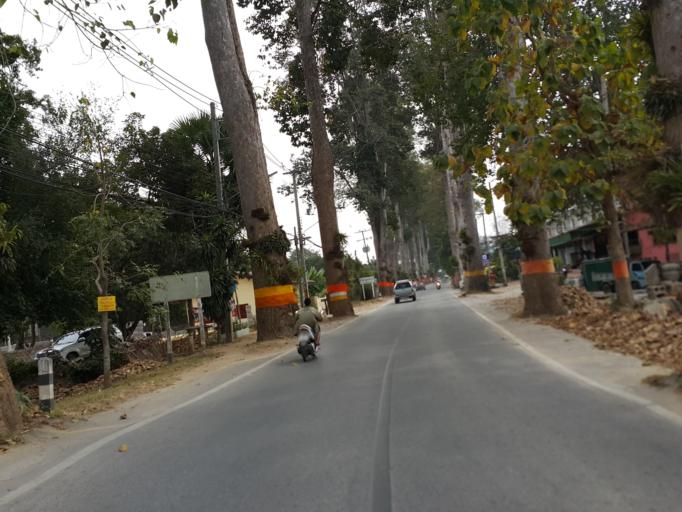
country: TH
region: Chiang Mai
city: Saraphi
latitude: 18.7008
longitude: 99.0431
